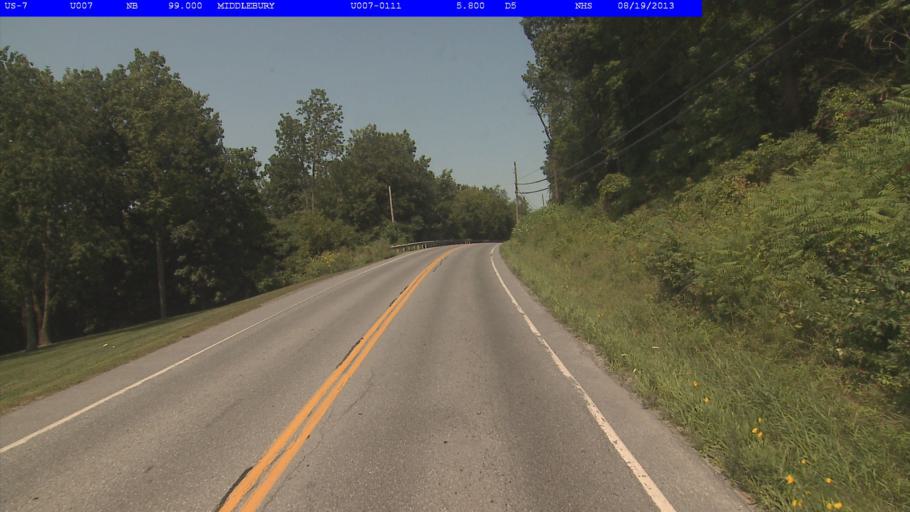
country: US
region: Vermont
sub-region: Addison County
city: Middlebury (village)
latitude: 44.0242
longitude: -73.1665
